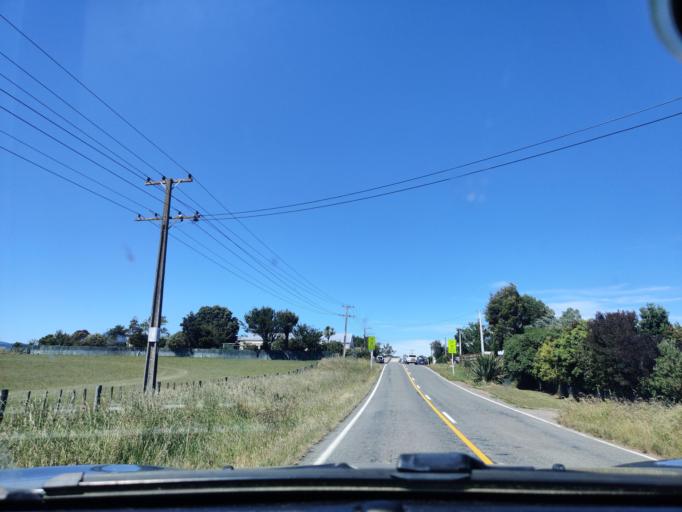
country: NZ
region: Wellington
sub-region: Upper Hutt City
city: Upper Hutt
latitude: -41.3510
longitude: 175.2062
